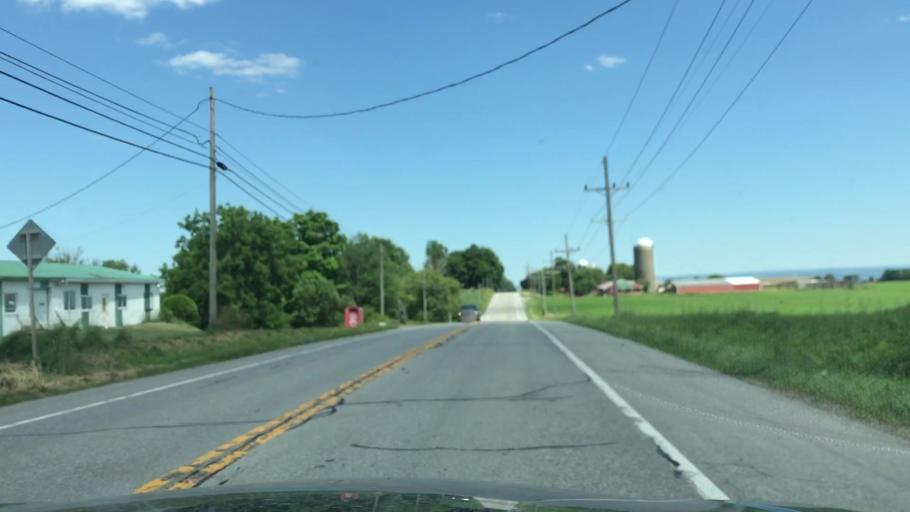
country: US
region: New York
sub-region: Wyoming County
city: Perry
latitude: 42.7473
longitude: -78.0231
